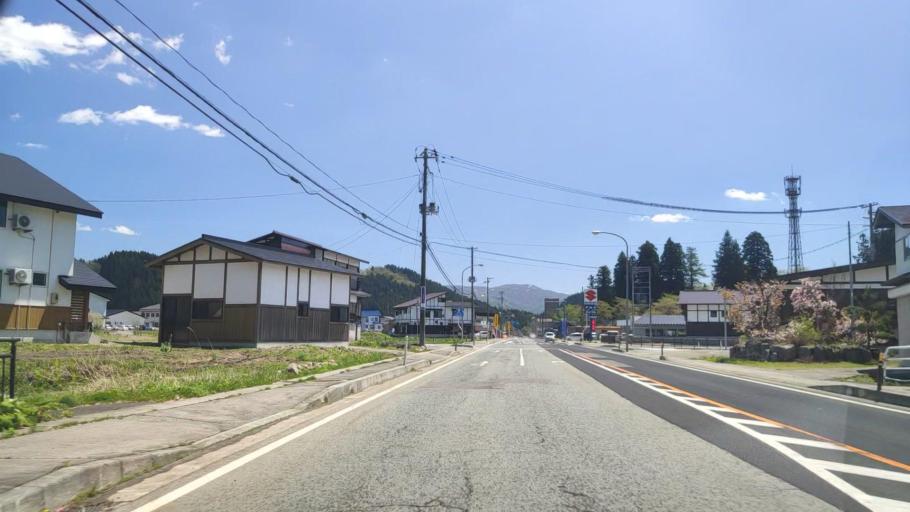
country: JP
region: Yamagata
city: Shinjo
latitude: 38.8885
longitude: 140.3316
